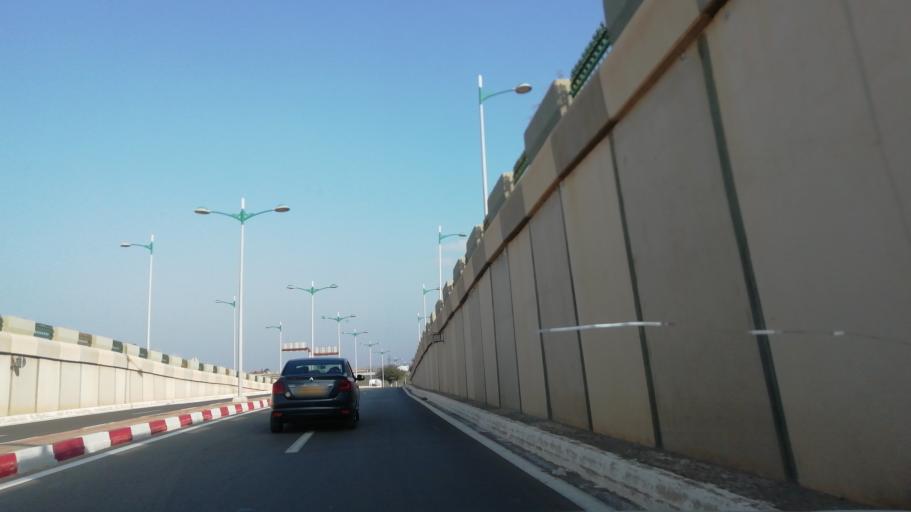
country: DZ
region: Ain Temouchent
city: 'Ain Temouchent
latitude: 35.2922
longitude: -1.1213
